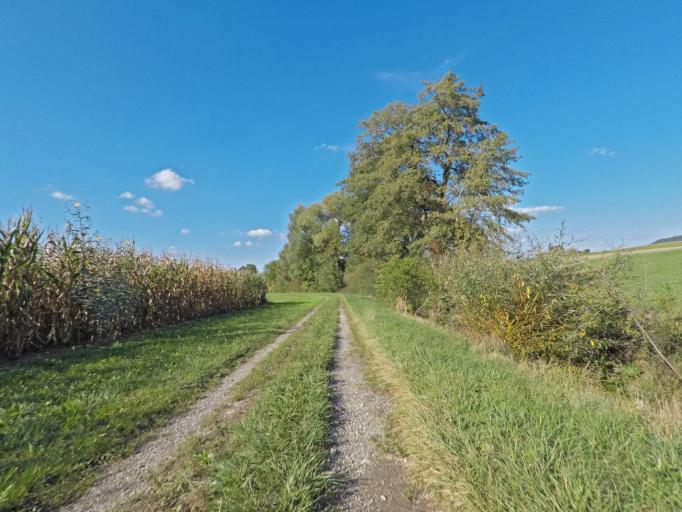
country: CH
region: Thurgau
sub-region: Frauenfeld District
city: Diessenhofen
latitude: 47.6614
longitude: 8.7472
